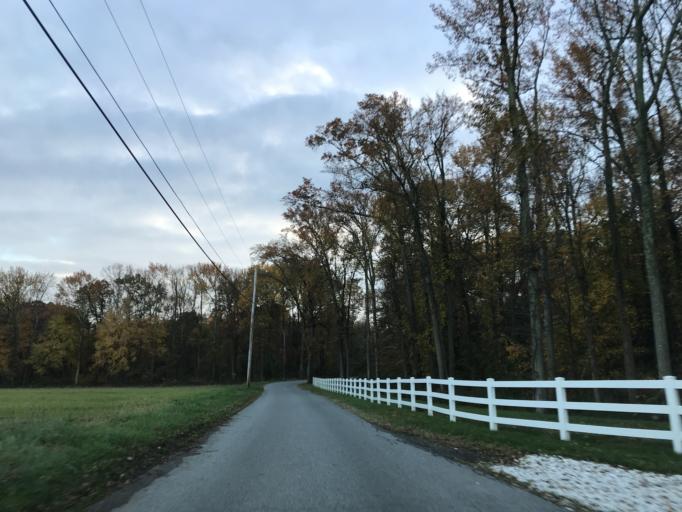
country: US
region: Maryland
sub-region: Baltimore County
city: Bowleys Quarters
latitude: 39.3689
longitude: -76.3998
